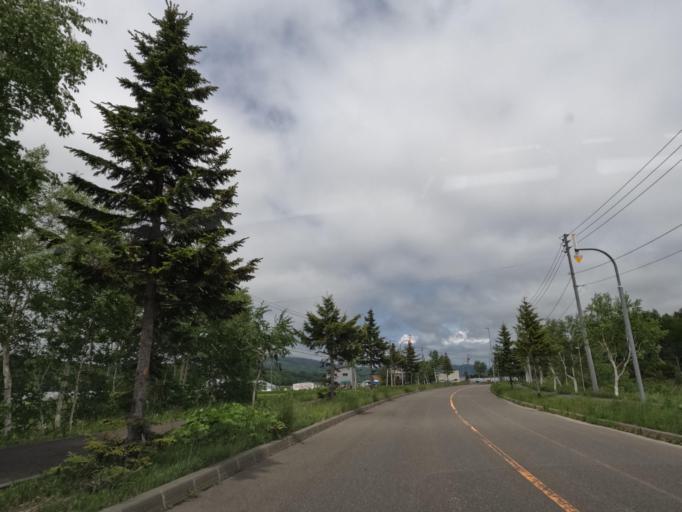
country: JP
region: Hokkaido
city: Tobetsu
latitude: 43.2588
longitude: 141.5238
